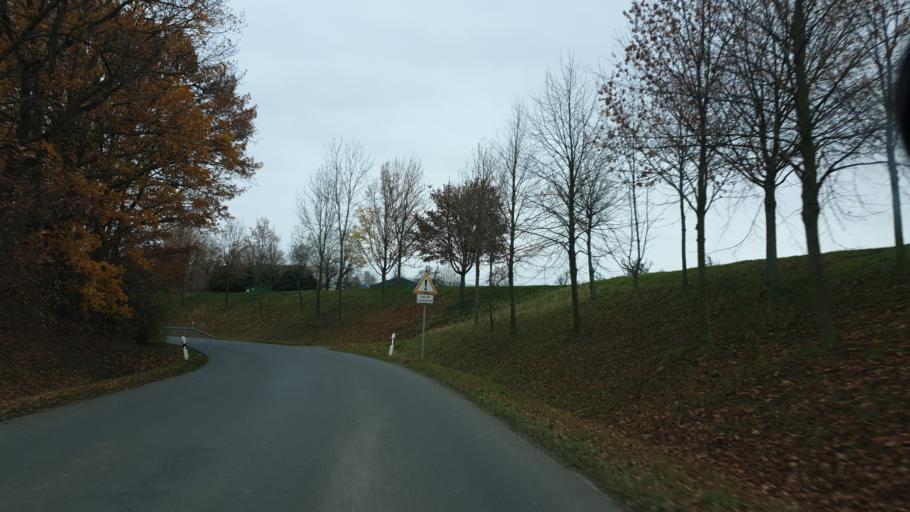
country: DE
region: Thuringia
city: Rauda
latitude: 50.9796
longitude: 11.9400
